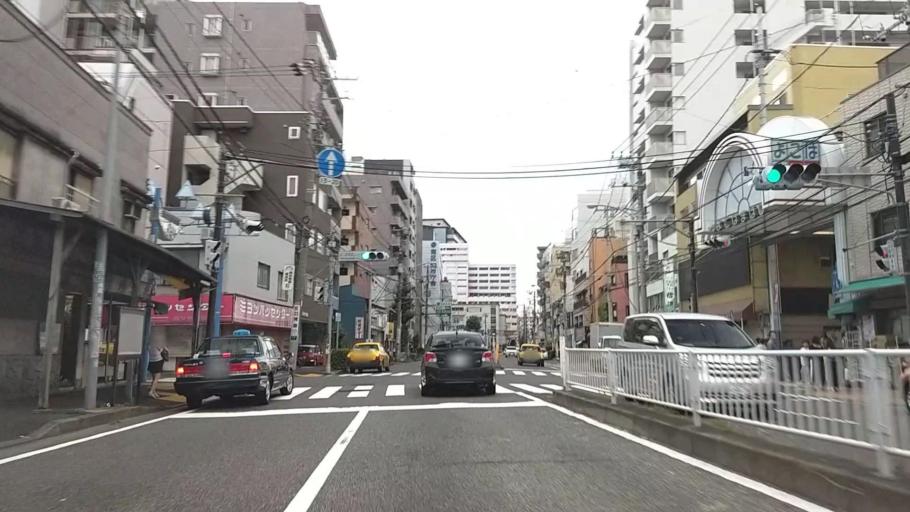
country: JP
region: Kanagawa
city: Yokohama
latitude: 35.4355
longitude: 139.6295
